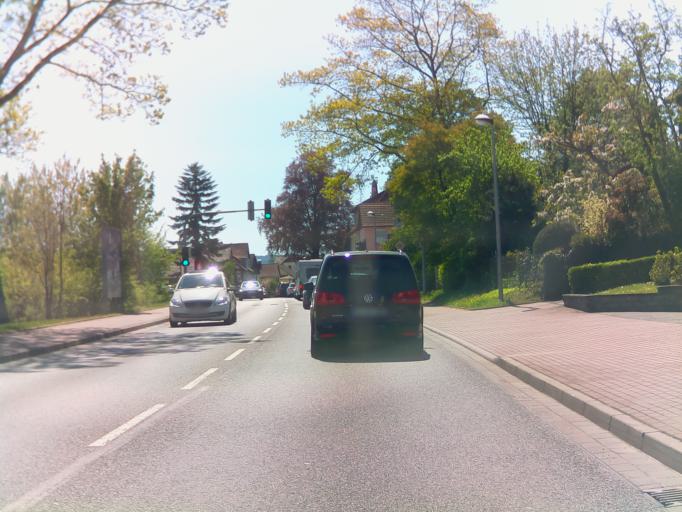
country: DE
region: Hesse
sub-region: Regierungsbezirk Kassel
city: Niederaula
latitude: 50.8043
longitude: 9.6139
